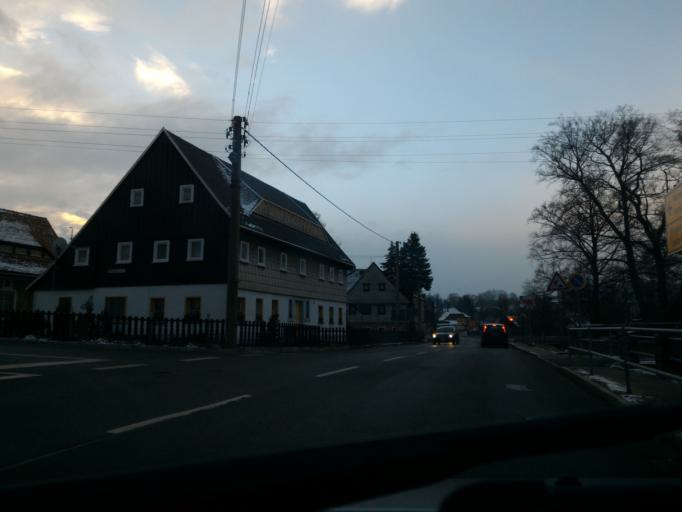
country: DE
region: Saxony
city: Seifhennersdorf
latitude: 50.9350
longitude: 14.6188
